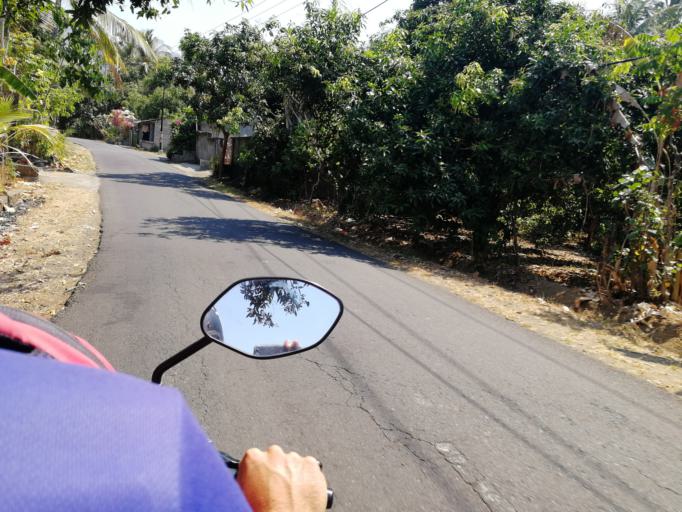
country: ID
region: Bali
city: Banjar Trunyan
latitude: -8.1227
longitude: 115.3286
